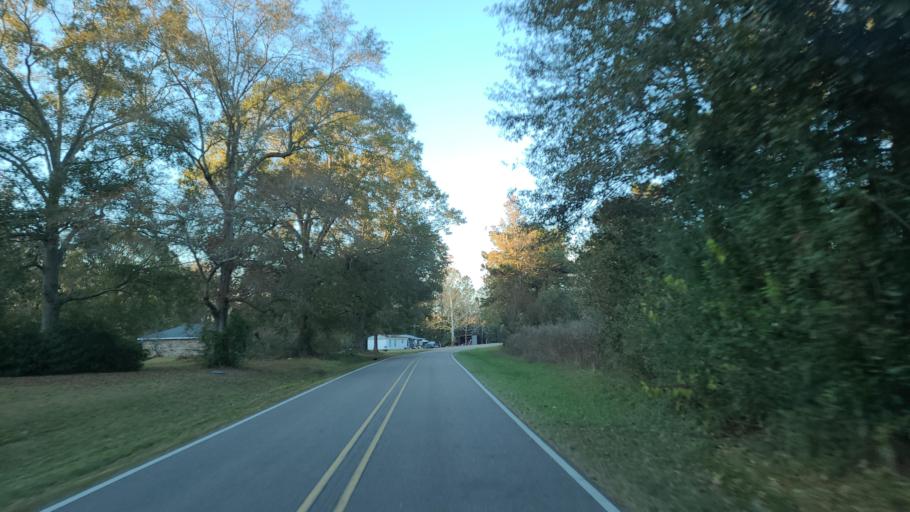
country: US
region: Mississippi
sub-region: Stone County
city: Wiggins
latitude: 30.9900
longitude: -89.2597
